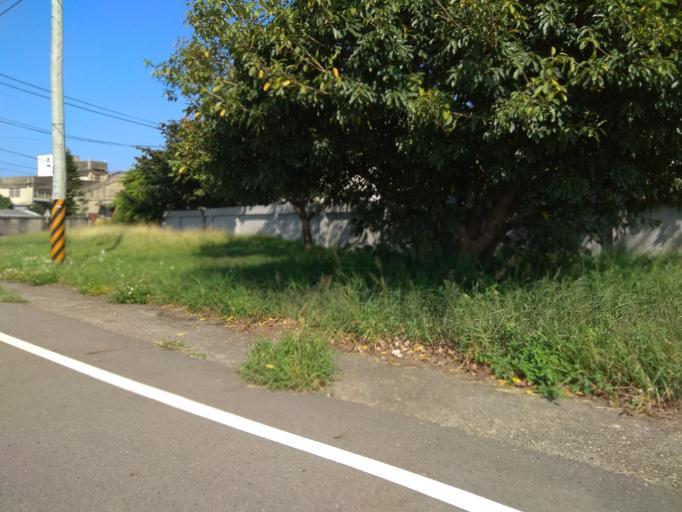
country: TW
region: Taiwan
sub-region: Hsinchu
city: Zhubei
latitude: 24.9822
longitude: 121.0355
